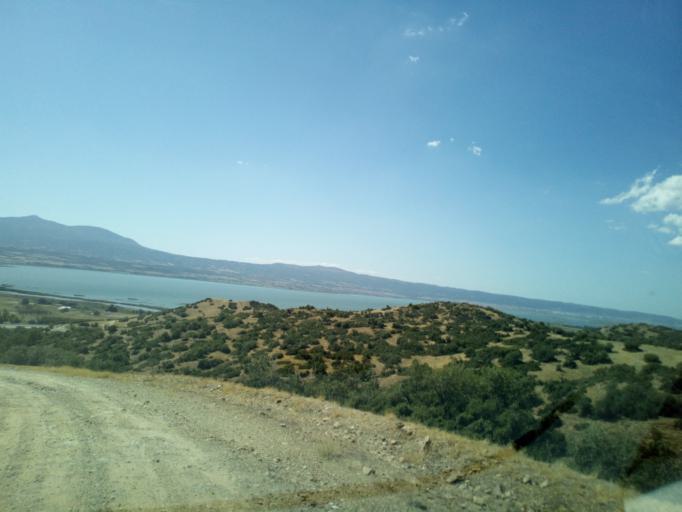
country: GR
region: Central Macedonia
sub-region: Nomos Thessalonikis
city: Gerakarou
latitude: 40.7040
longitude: 23.2165
